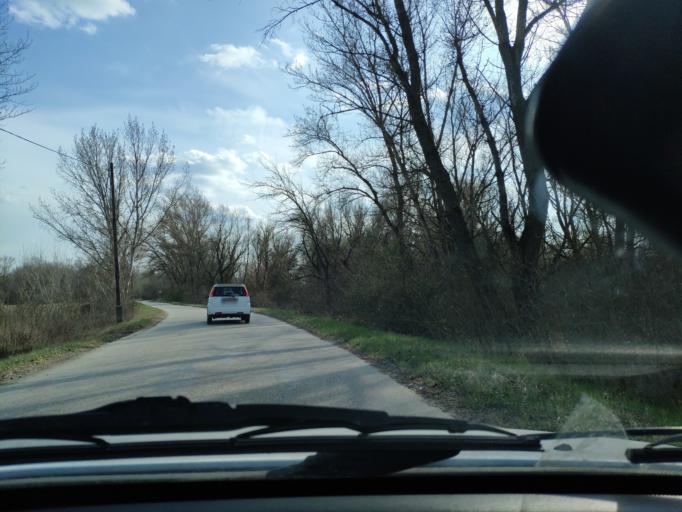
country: HU
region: Fejer
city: Adony
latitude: 47.1168
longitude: 18.8897
